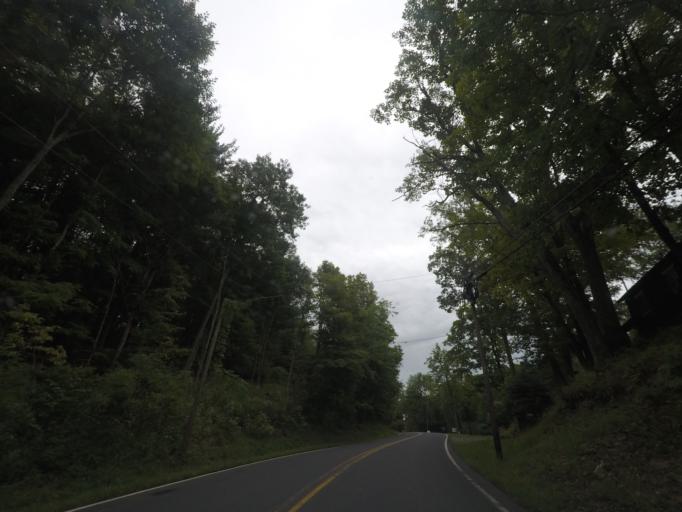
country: US
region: New York
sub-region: Rensselaer County
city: Nassau
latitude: 42.4819
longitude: -73.5929
